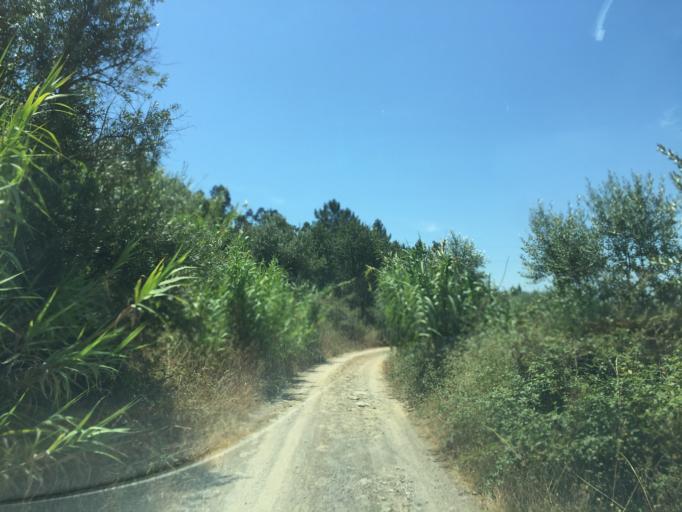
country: PT
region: Santarem
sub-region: Tomar
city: Tomar
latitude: 39.5979
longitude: -8.3572
